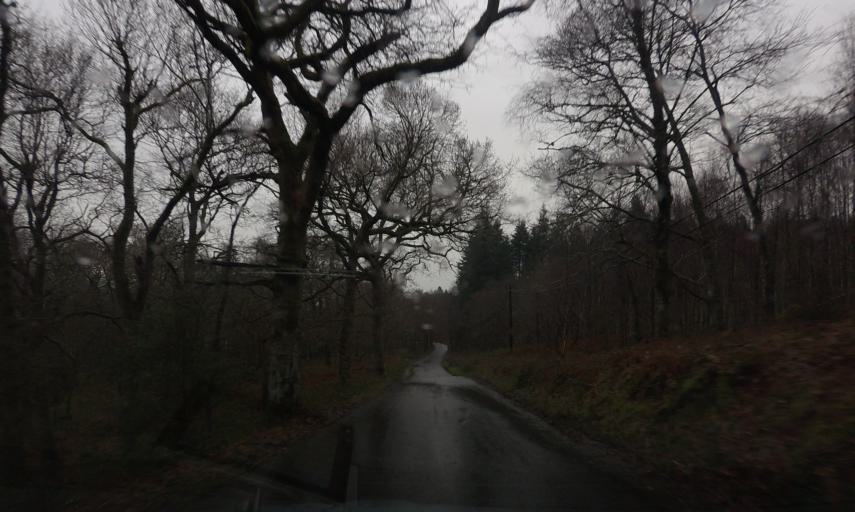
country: GB
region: Scotland
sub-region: West Dunbartonshire
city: Balloch
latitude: 56.1247
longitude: -4.6018
